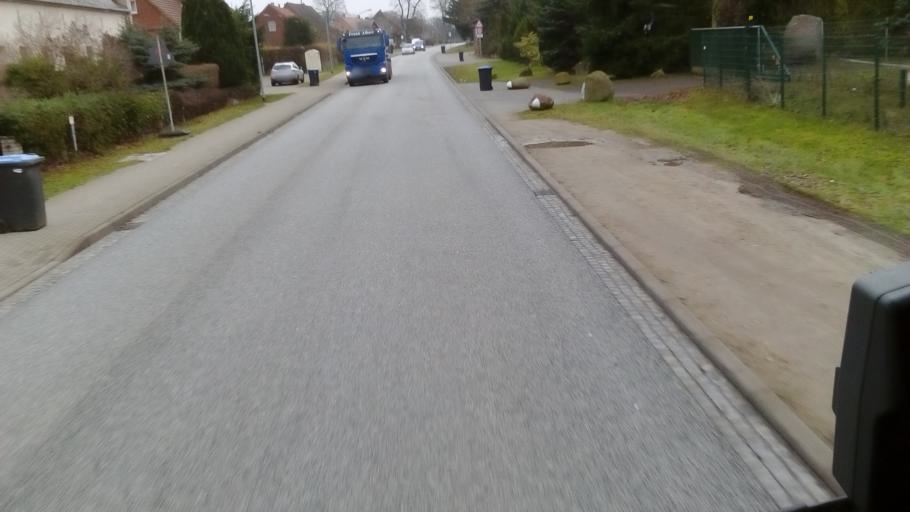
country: DE
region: Brandenburg
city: Pritzwalk
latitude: 53.1404
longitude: 12.2341
